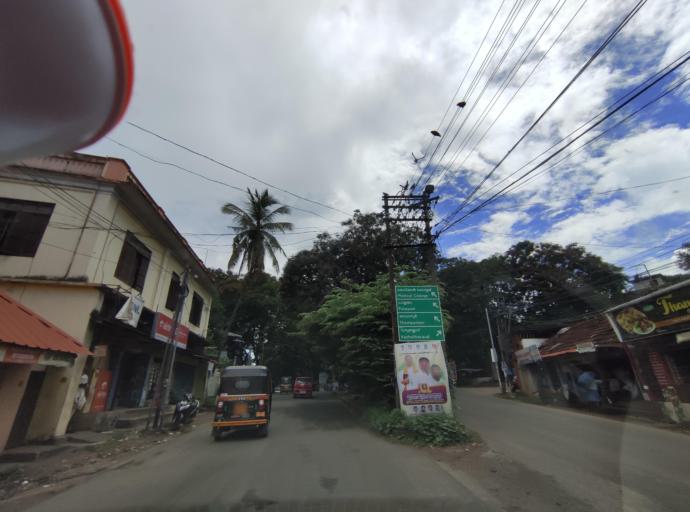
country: IN
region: Kerala
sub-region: Thiruvananthapuram
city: Thiruvananthapuram
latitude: 8.4957
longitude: 76.9626
